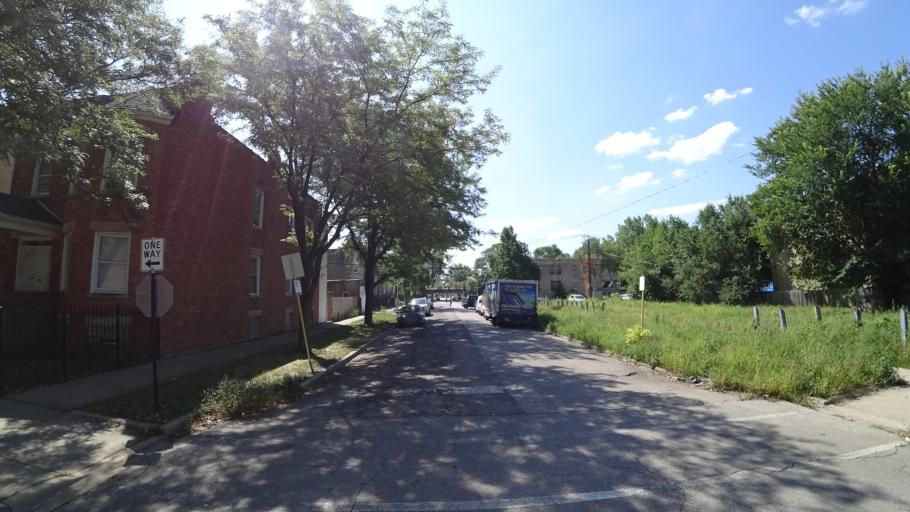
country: US
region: Illinois
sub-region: Cook County
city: Cicero
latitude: 41.8698
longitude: -87.7229
